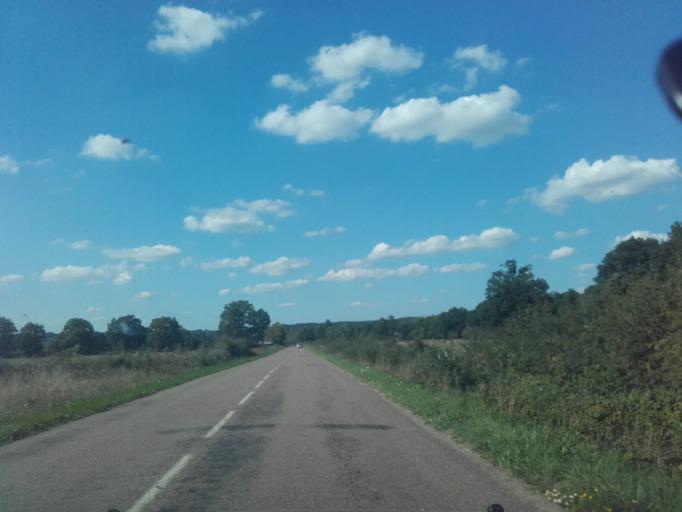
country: FR
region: Bourgogne
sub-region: Departement de Saone-et-Loire
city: Epinac
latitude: 46.9994
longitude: 4.4784
